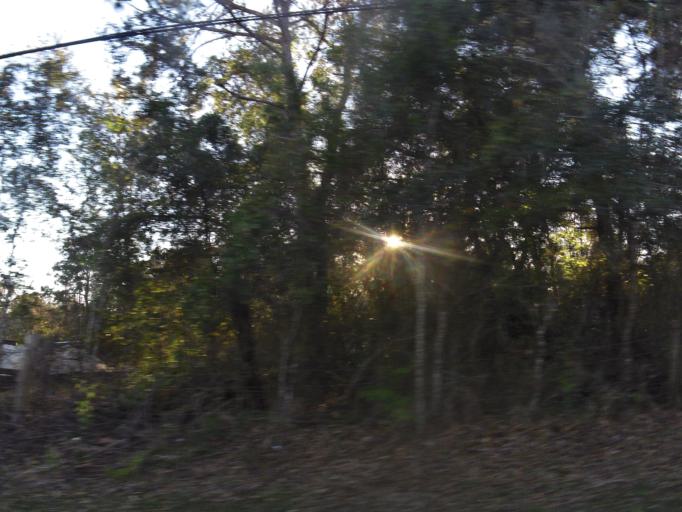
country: US
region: Florida
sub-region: Saint Johns County
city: Fruit Cove
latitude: 30.2008
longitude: -81.5754
